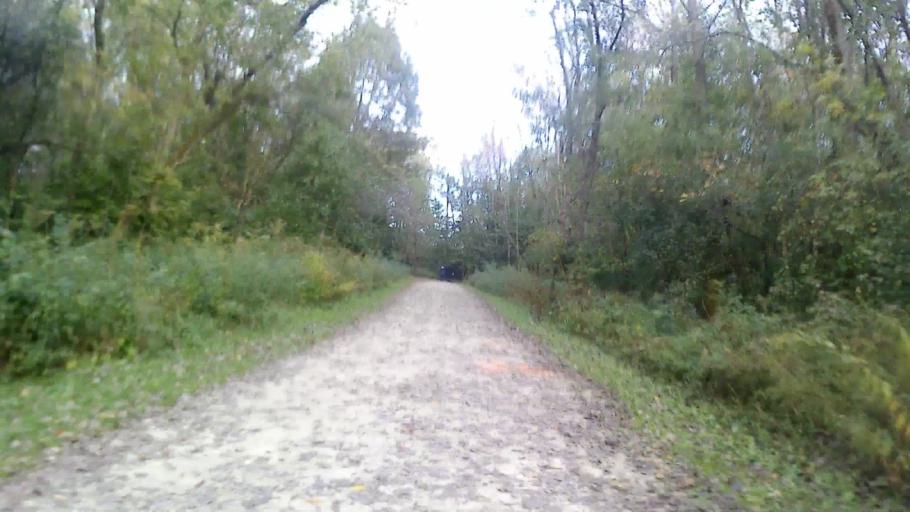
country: US
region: Illinois
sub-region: DuPage County
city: Warrenville
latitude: 41.8257
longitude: -88.1420
